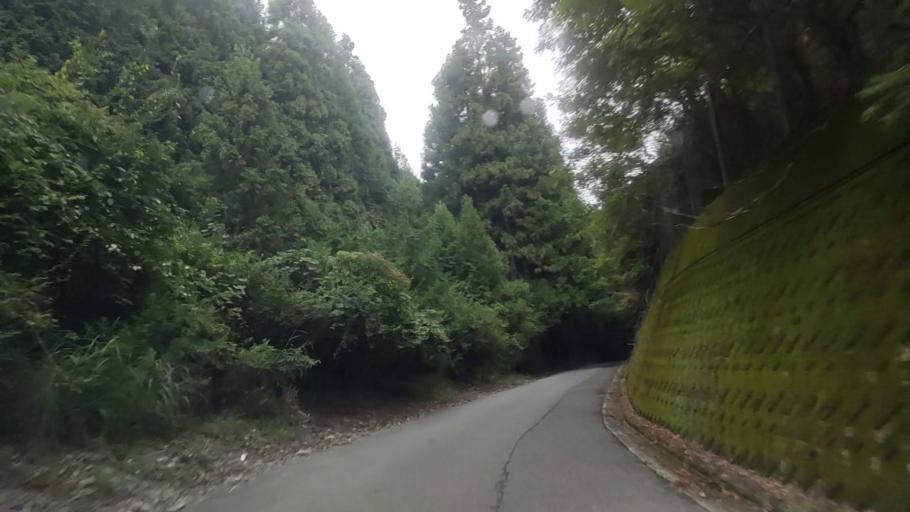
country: JP
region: Wakayama
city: Hashimoto
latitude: 34.2934
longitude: 135.6295
